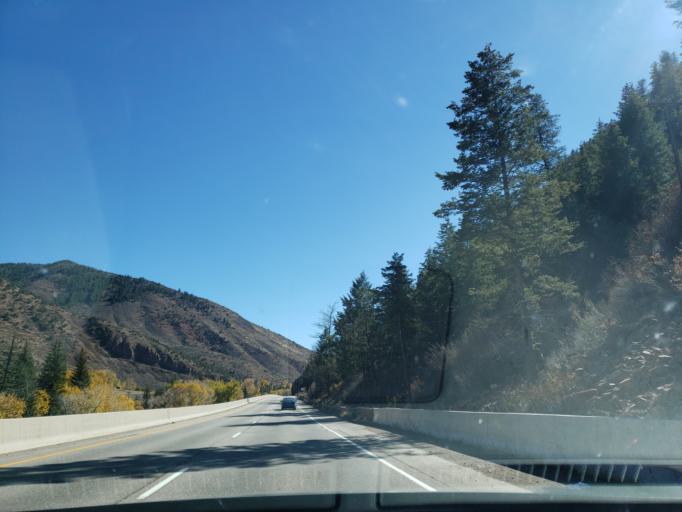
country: US
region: Colorado
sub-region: Eagle County
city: Basalt
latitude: 39.3197
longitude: -106.9443
